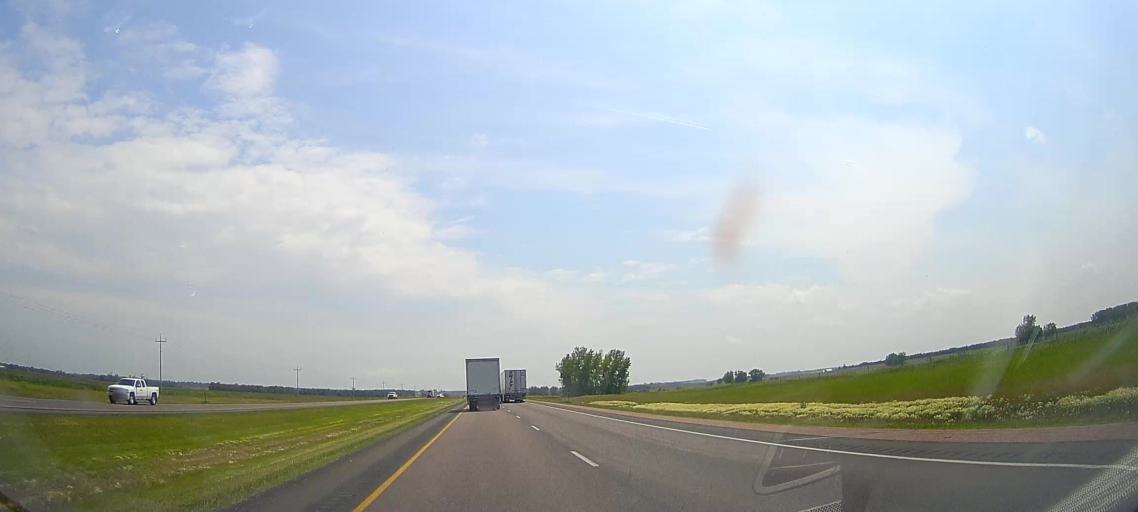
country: US
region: South Dakota
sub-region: Union County
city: Beresford
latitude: 43.1123
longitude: -96.7967
